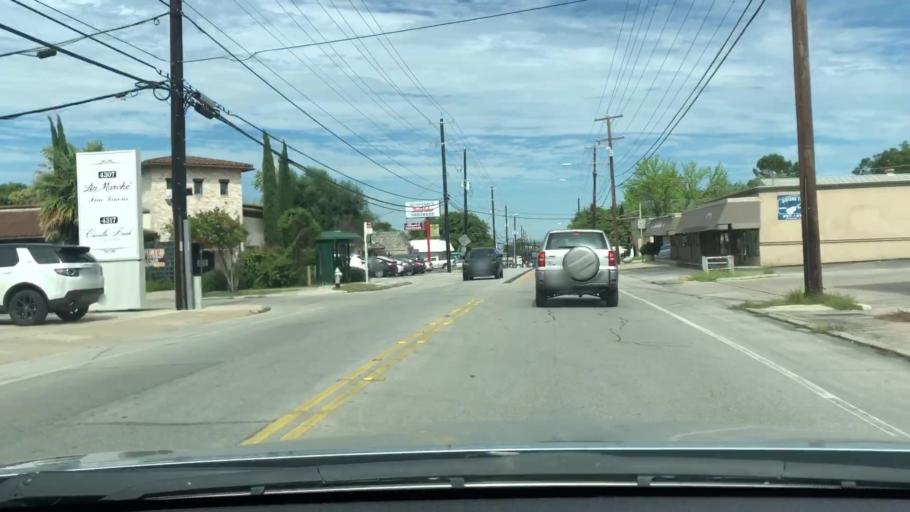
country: US
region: Texas
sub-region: Bexar County
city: Olmos Park
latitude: 29.4713
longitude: -98.4917
